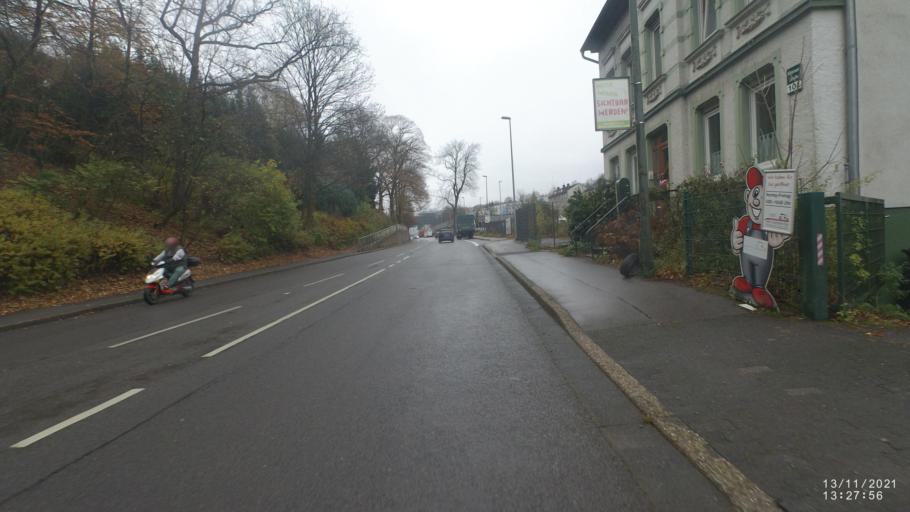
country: DE
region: North Rhine-Westphalia
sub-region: Regierungsbezirk Arnsberg
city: Luedenscheid
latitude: 51.2313
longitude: 7.6329
